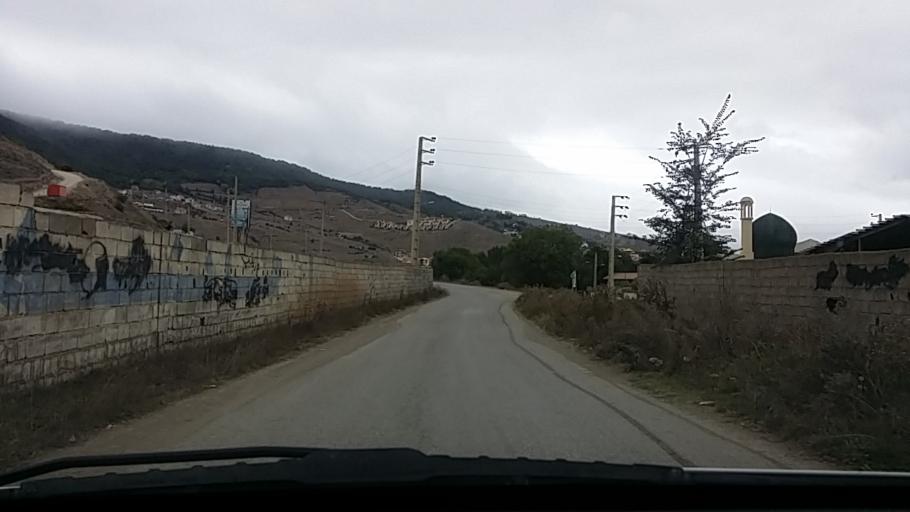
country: IR
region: Mazandaran
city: `Abbasabad
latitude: 36.5124
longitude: 51.1609
